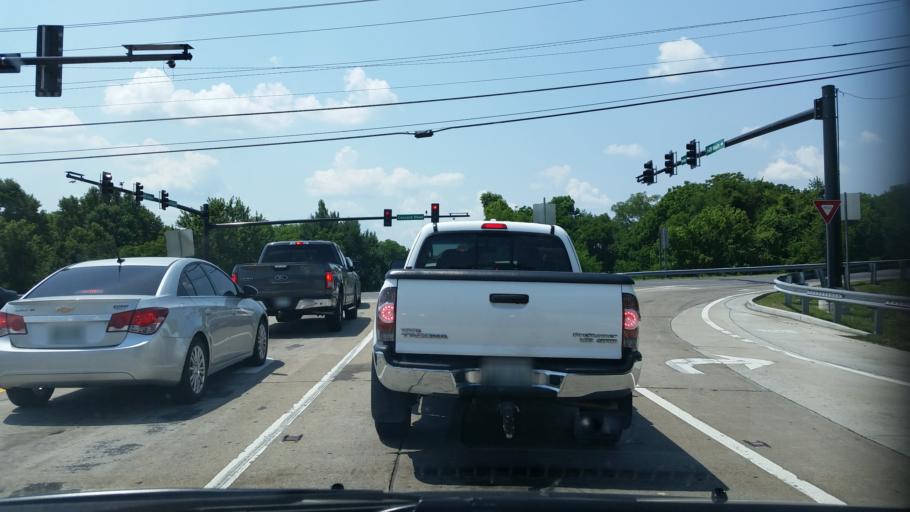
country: US
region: Tennessee
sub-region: Williamson County
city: Brentwood Estates
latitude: 35.9982
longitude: -86.7989
